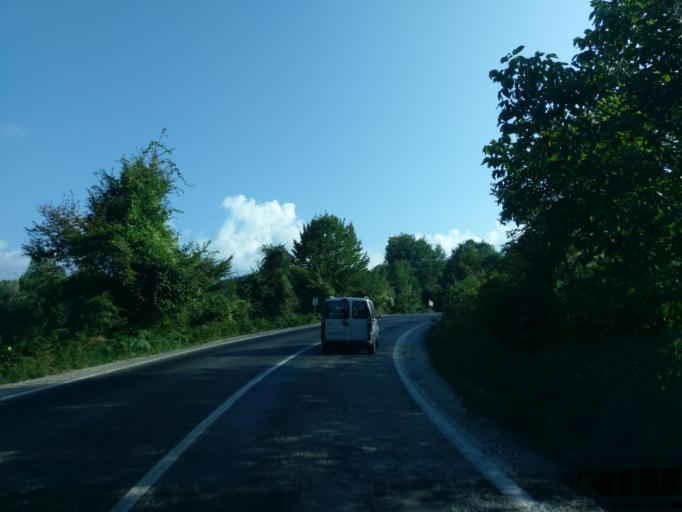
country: TR
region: Sinop
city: Ayancik
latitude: 41.8796
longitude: 34.5203
